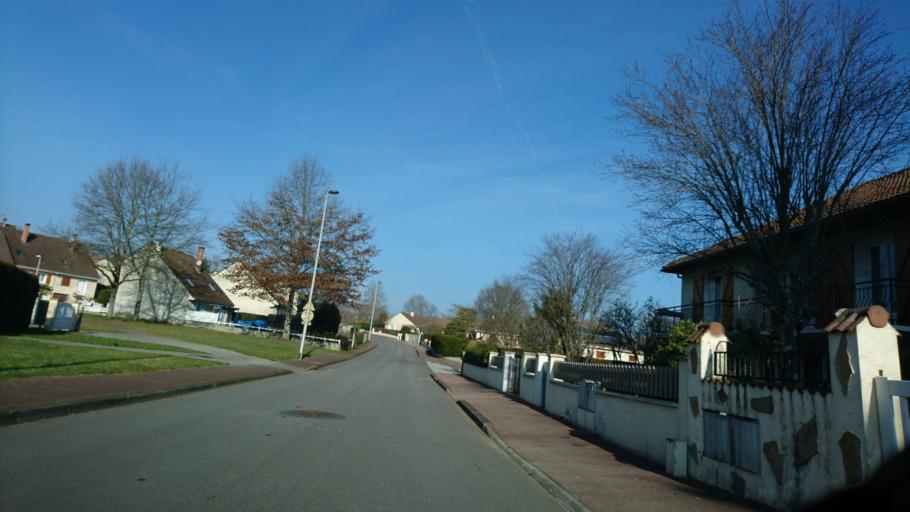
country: FR
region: Limousin
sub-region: Departement de la Haute-Vienne
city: Rilhac-Rancon
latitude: 45.8803
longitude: 1.3026
